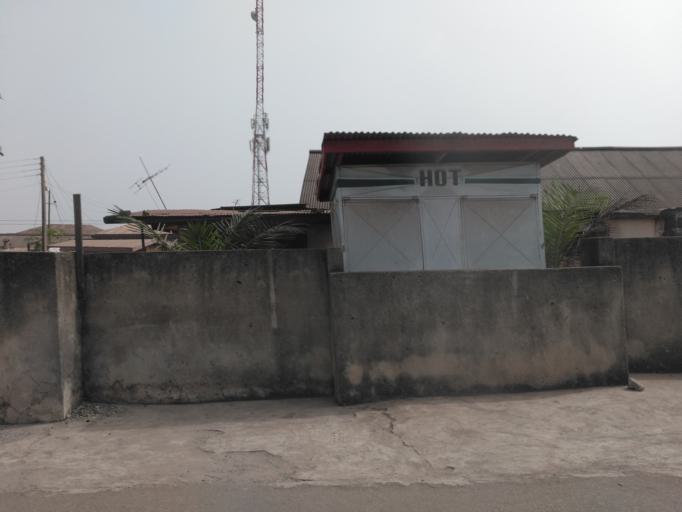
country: GH
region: Ashanti
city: Kumasi
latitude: 6.7041
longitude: -1.6079
